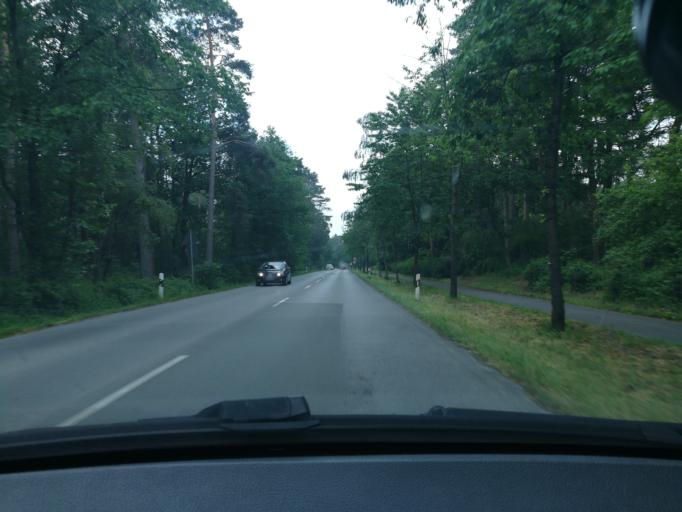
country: DE
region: North Rhine-Westphalia
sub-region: Regierungsbezirk Detmold
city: Oerlinghausen
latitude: 51.9254
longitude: 8.6561
